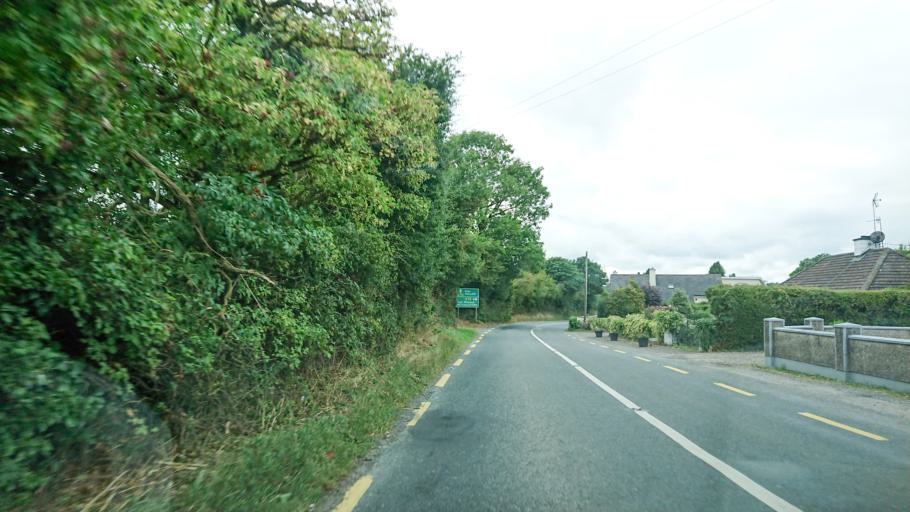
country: IE
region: Munster
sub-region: County Cork
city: Mallow
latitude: 52.1489
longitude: -8.6135
